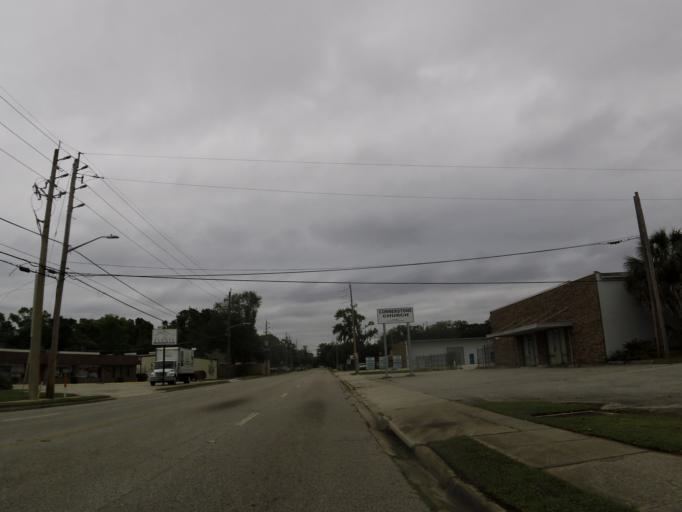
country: US
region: Florida
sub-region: Duval County
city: Jacksonville
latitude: 30.2725
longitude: -81.6382
